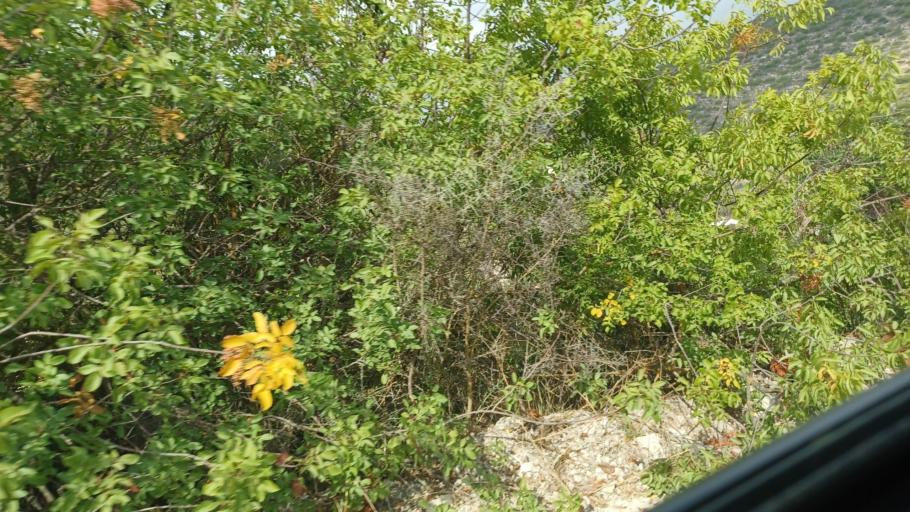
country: CY
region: Pafos
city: Tala
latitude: 34.8739
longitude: 32.4581
